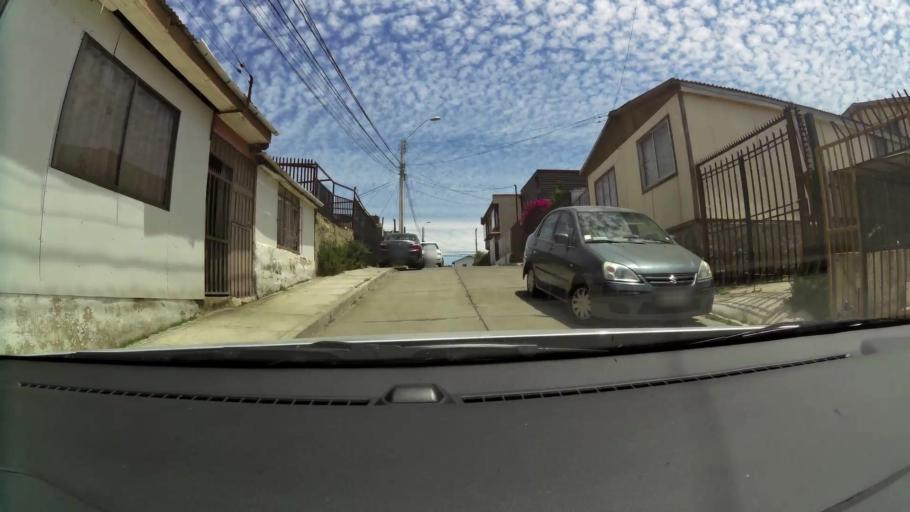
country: CL
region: Valparaiso
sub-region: Provincia de Valparaiso
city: Vina del Mar
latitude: -33.0501
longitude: -71.5731
